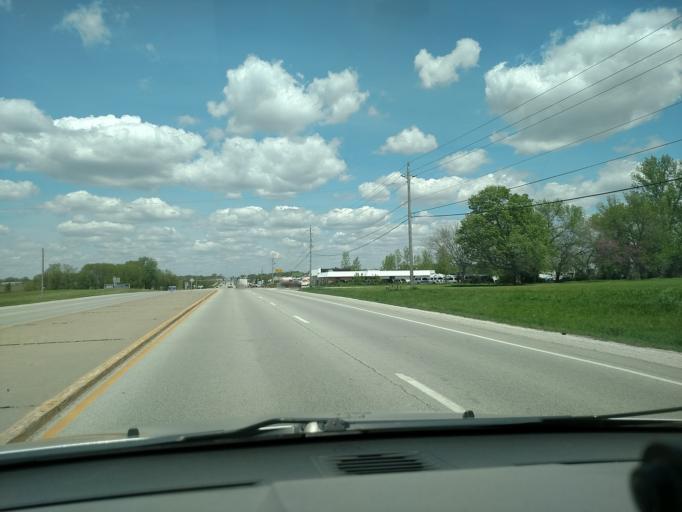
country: US
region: Iowa
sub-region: Polk County
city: Ankeny
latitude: 41.7055
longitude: -93.6005
